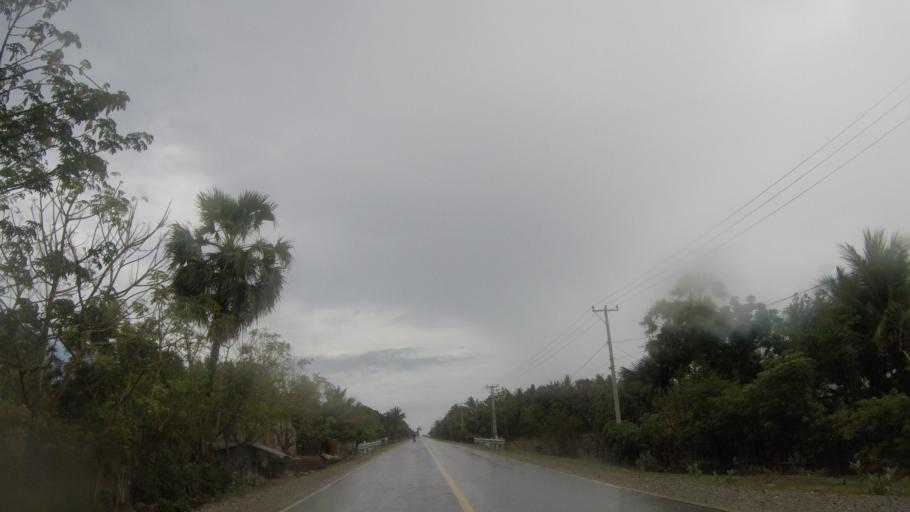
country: TL
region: Lautem
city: Lospalos
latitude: -8.3755
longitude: 126.8726
